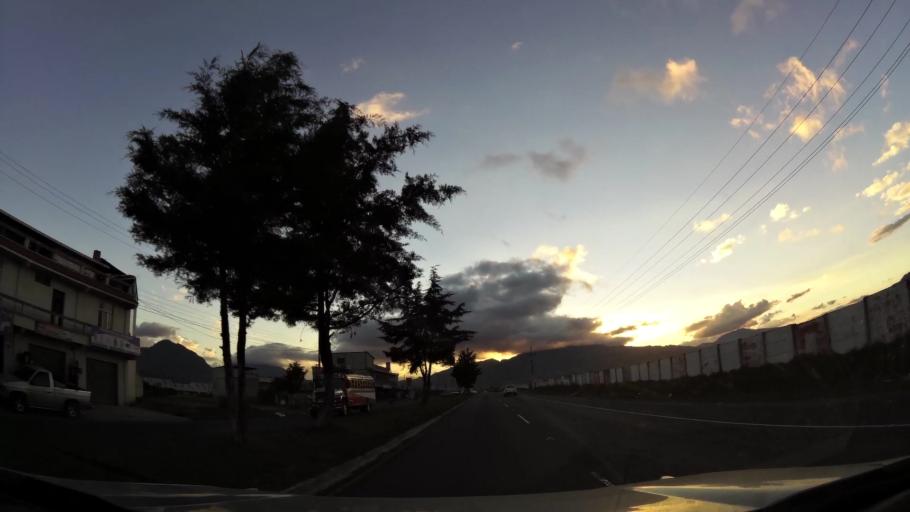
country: GT
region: Quetzaltenango
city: Olintepeque
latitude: 14.8628
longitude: -91.5041
